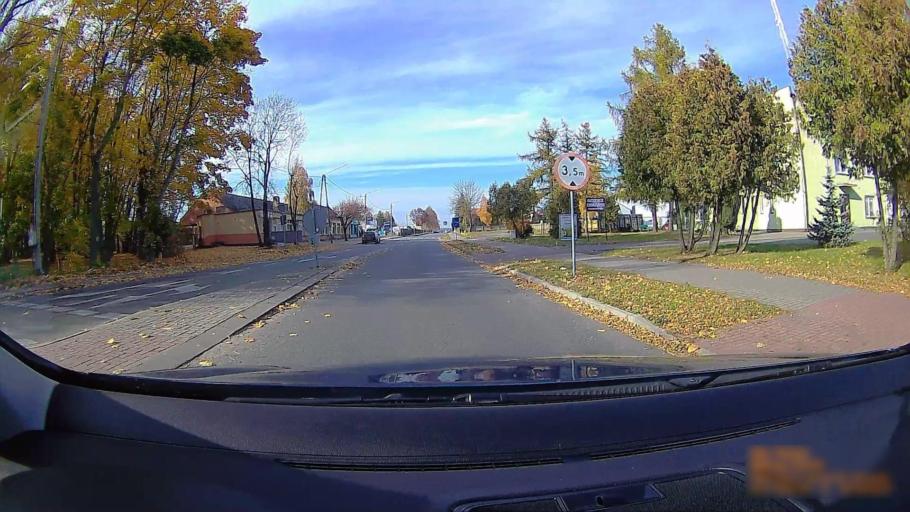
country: PL
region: Greater Poland Voivodeship
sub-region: Powiat ostrzeszowski
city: Doruchow
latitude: 51.4167
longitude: 18.0762
